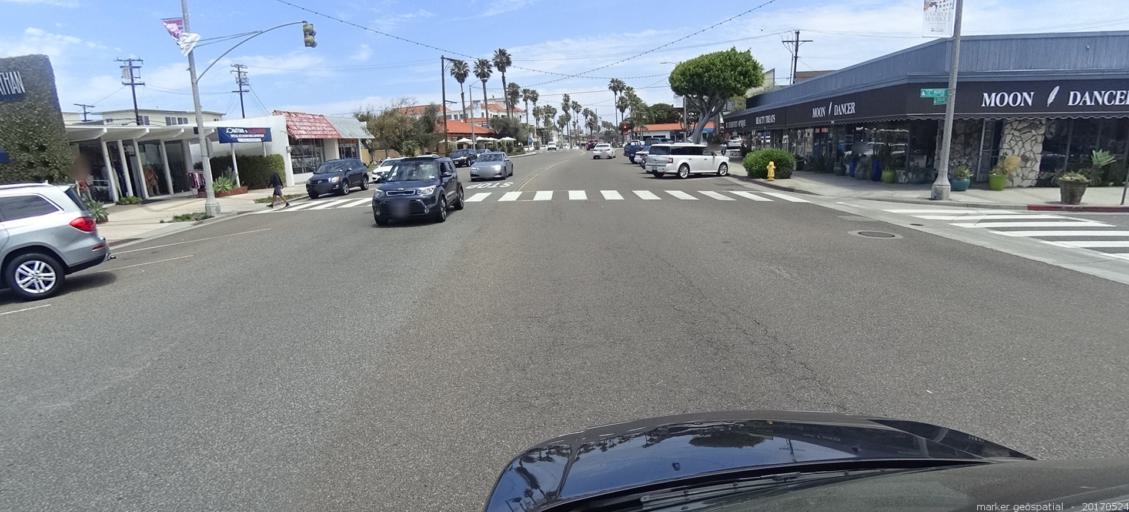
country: US
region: California
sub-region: Los Angeles County
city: Palos Verdes Estates
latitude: 33.8182
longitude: -118.3880
